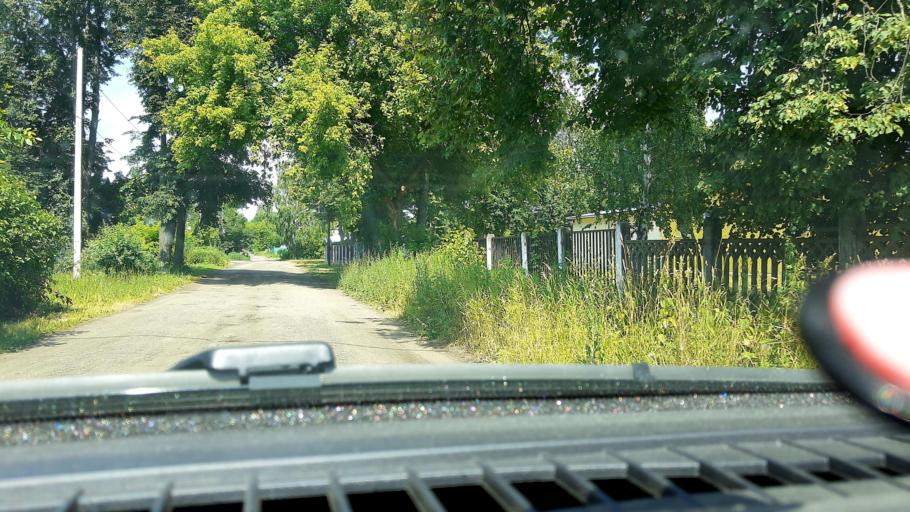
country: RU
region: Nizjnij Novgorod
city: Gorbatovka
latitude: 56.2702
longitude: 43.7518
